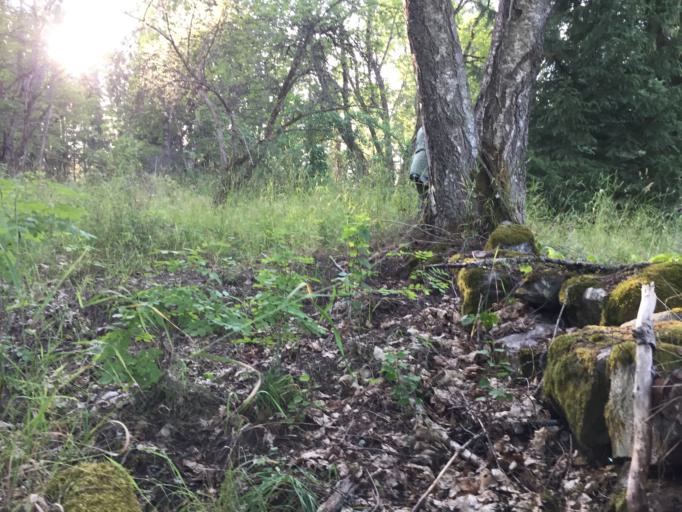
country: SE
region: Stockholm
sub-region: Salems Kommun
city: Ronninge
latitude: 59.2451
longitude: 17.6820
